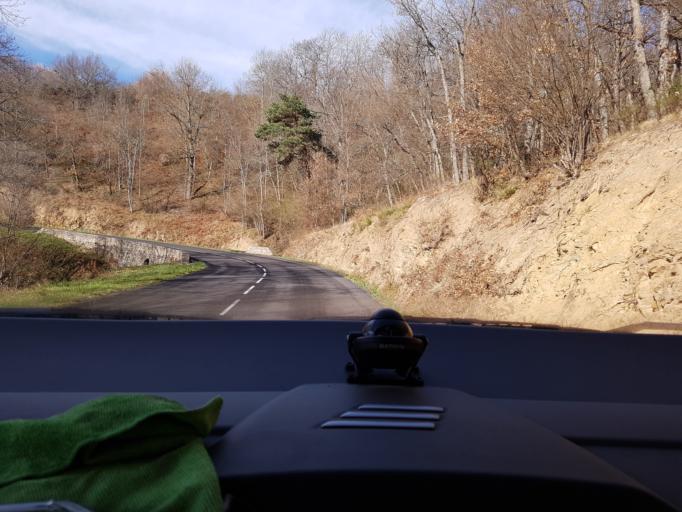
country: FR
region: Auvergne
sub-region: Departement du Cantal
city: Massiac
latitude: 45.2311
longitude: 3.1962
